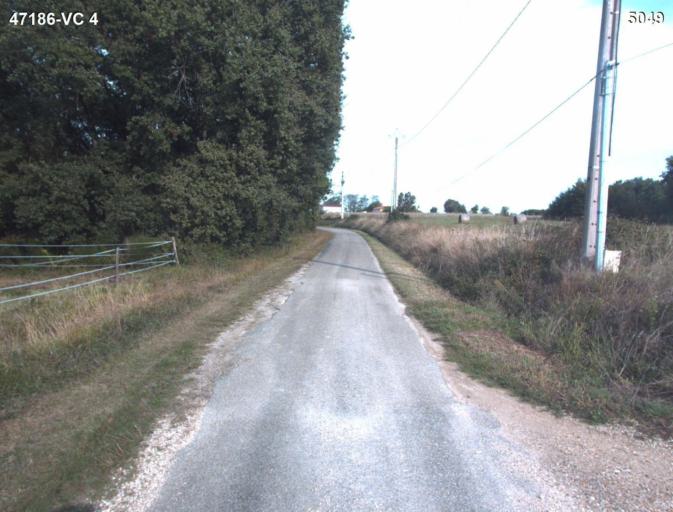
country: FR
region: Aquitaine
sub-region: Departement du Lot-et-Garonne
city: Sainte-Colombe-en-Bruilhois
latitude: 44.1904
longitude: 0.4572
